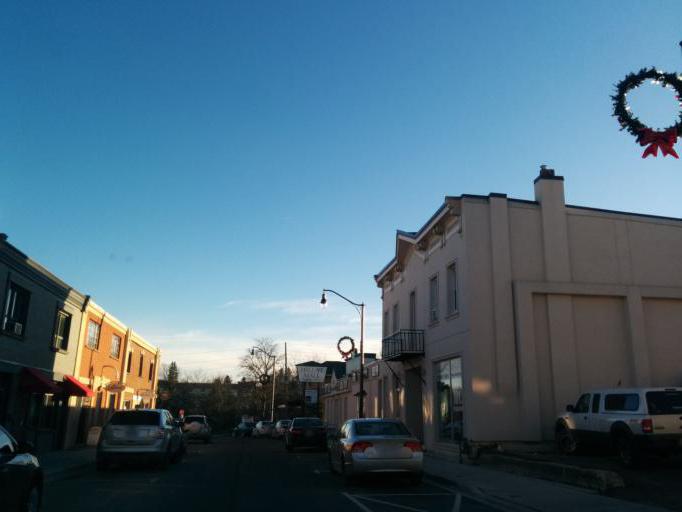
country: CA
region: Ontario
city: Orangeville
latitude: 43.9190
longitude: -80.0959
